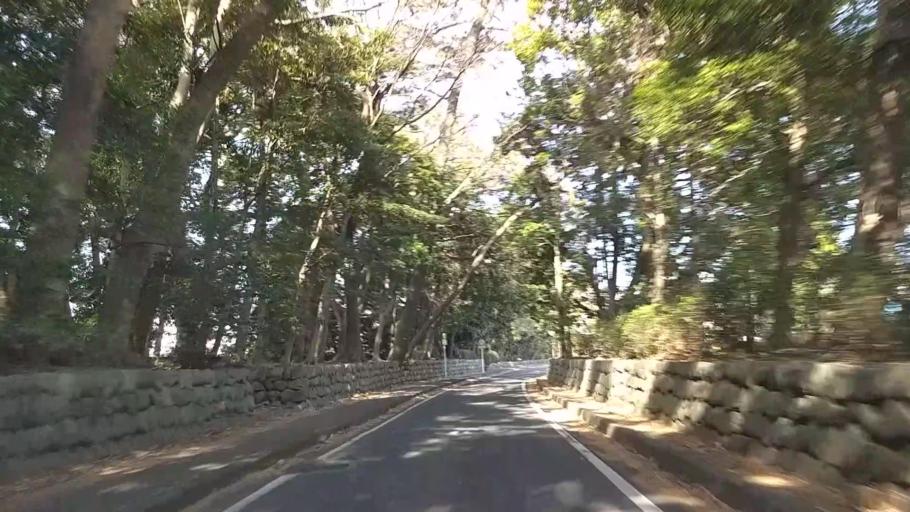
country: JP
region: Kanagawa
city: Chigasaki
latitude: 35.3745
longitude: 139.3806
